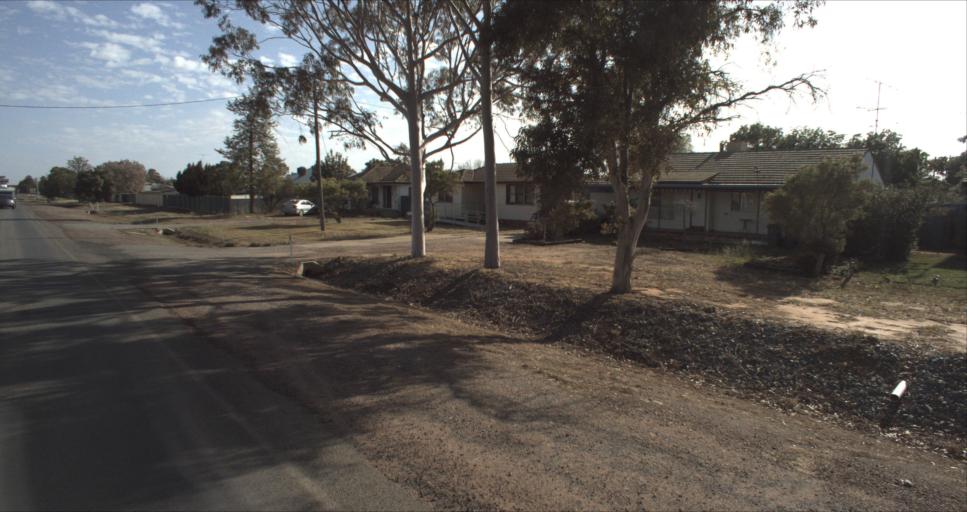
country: AU
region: New South Wales
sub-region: Leeton
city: Leeton
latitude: -34.5671
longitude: 146.3936
